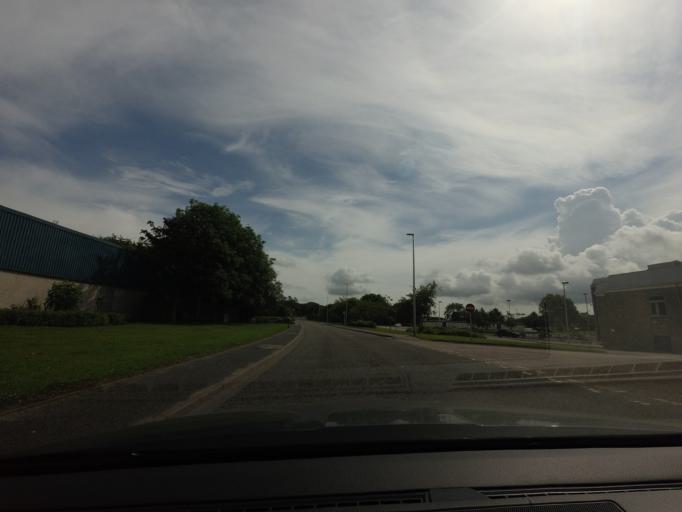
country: GB
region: Scotland
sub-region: Aberdeenshire
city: Mintlaw
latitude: 57.5253
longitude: -2.0138
